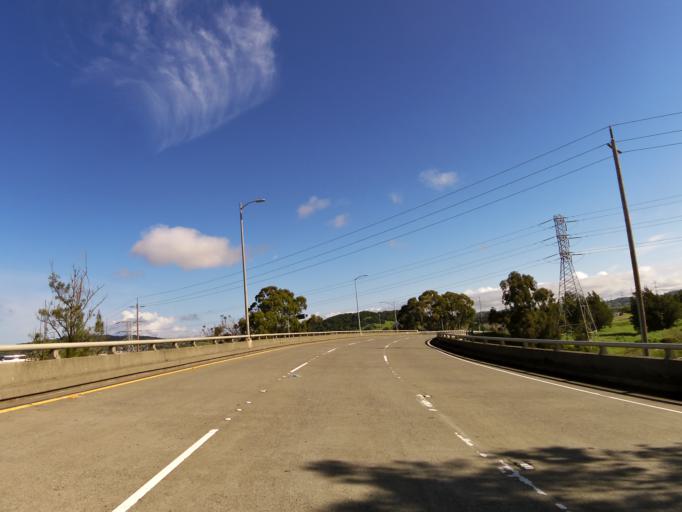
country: US
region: California
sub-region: Marin County
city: Novato
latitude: 38.0805
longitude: -122.5446
